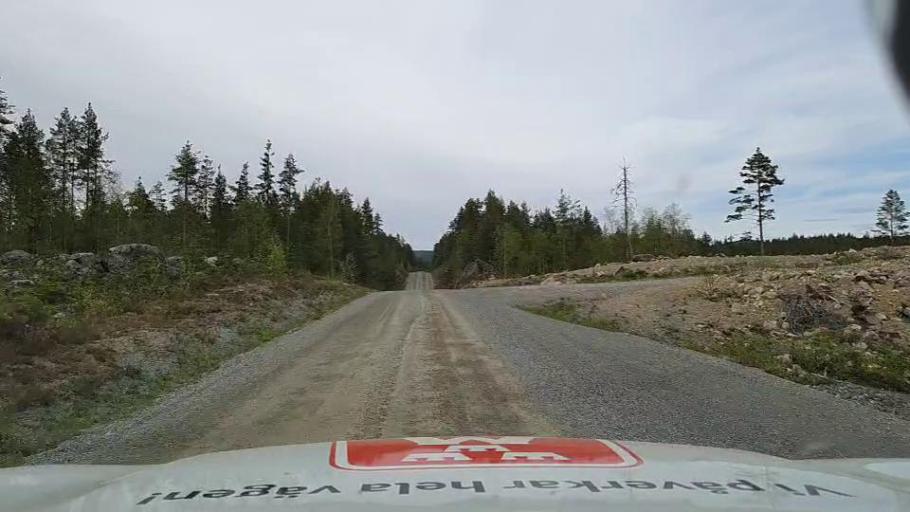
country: SE
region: Jaemtland
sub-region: Braecke Kommun
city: Braecke
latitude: 62.4745
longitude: 14.9165
